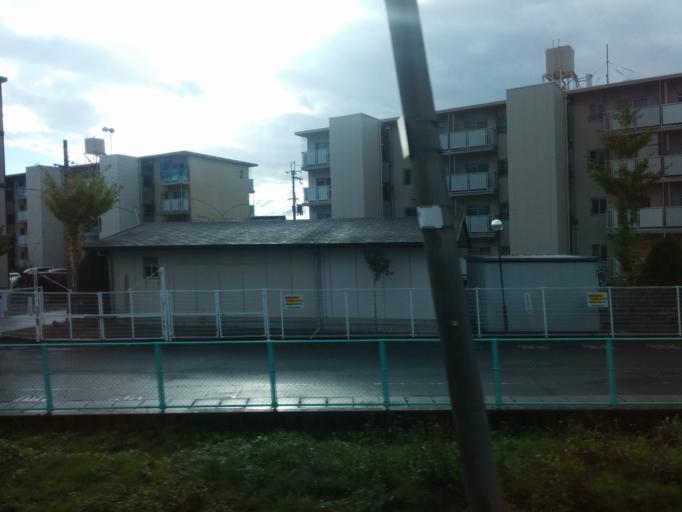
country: JP
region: Shiga Prefecture
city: Omihachiman
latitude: 35.1257
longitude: 136.1063
